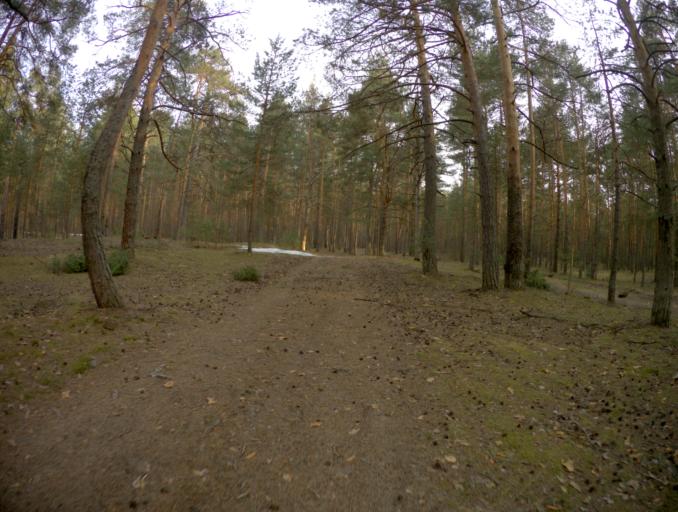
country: RU
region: Vladimir
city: Kommunar
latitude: 56.0810
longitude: 40.4372
